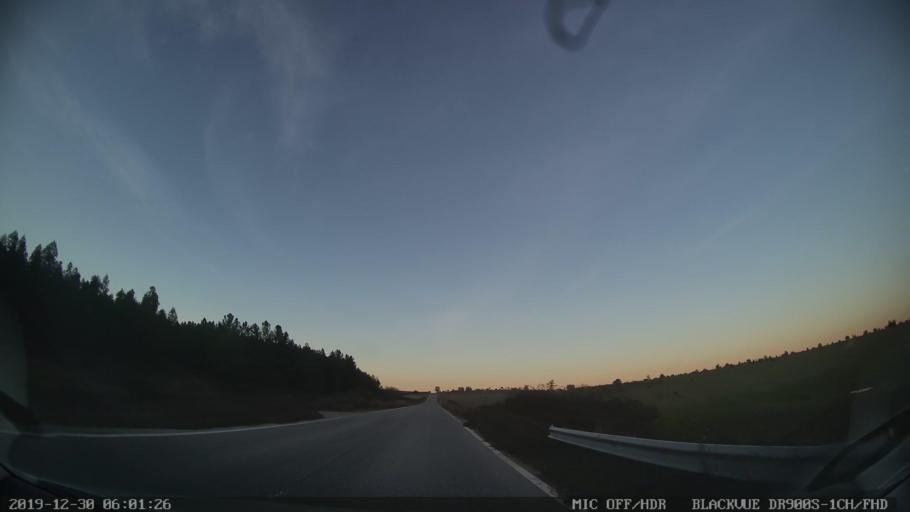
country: PT
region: Castelo Branco
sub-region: Penamacor
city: Penamacor
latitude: 40.0606
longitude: -7.2434
